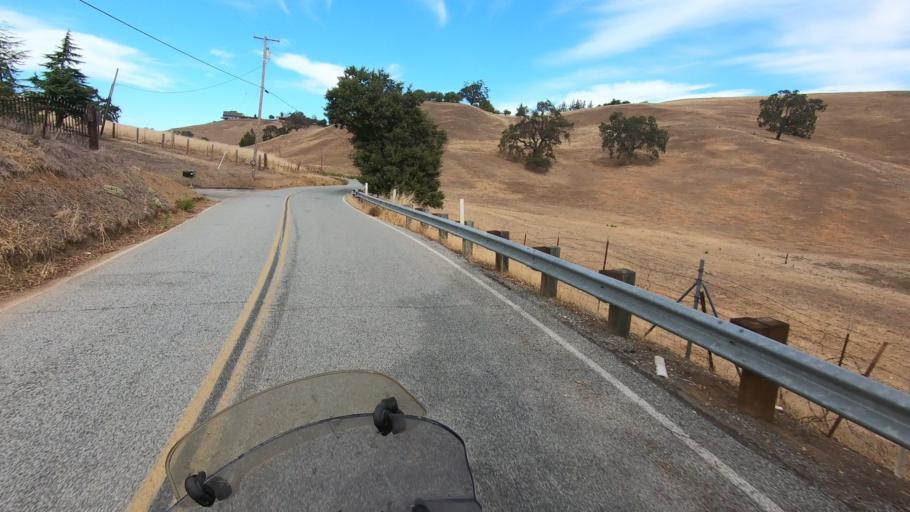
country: US
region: California
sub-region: Santa Clara County
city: East Foothills
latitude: 37.4166
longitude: -121.7794
